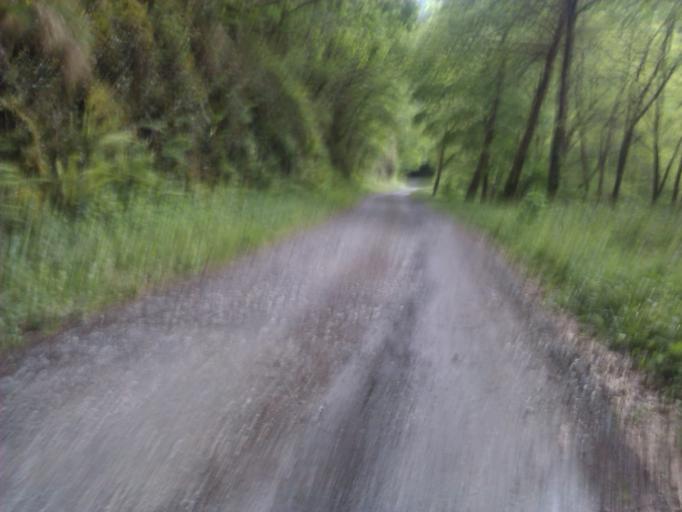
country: ES
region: Basque Country
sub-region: Provincia de Guipuzcoa
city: Berastegui
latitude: 43.1319
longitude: -1.9377
